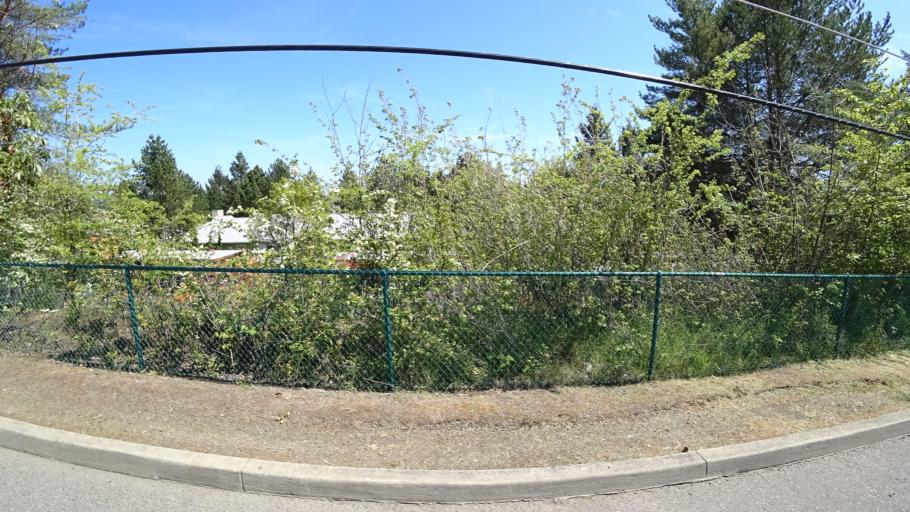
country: US
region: Oregon
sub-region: Washington County
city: King City
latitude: 45.4354
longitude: -122.8364
